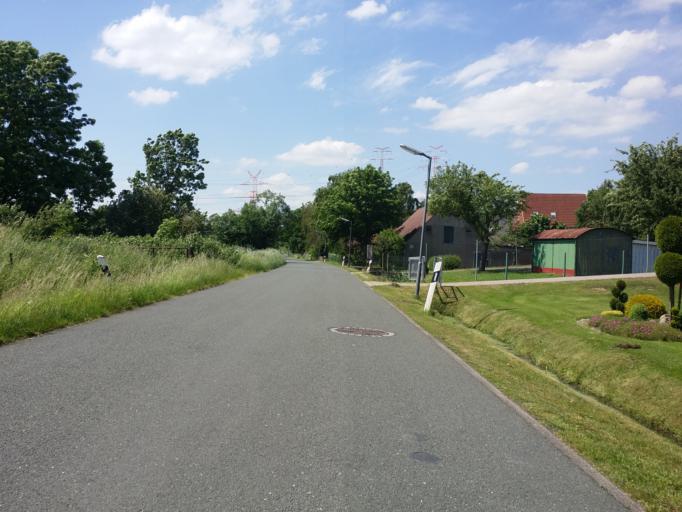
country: DE
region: Lower Saxony
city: Lemwerder
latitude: 53.1187
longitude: 8.6764
